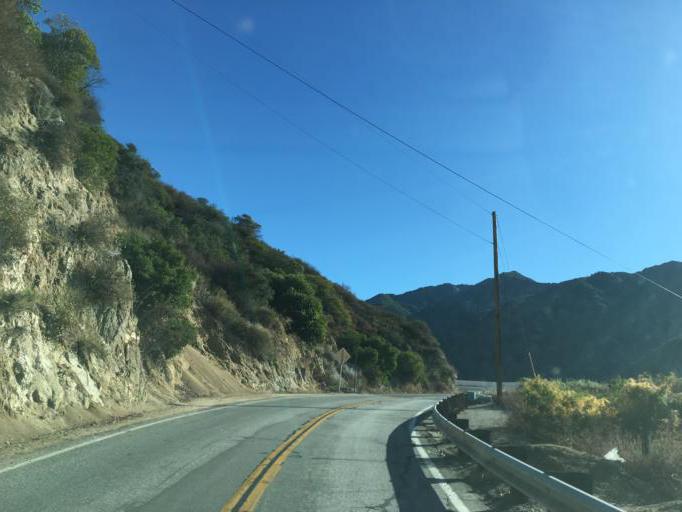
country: US
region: California
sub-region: Los Angeles County
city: Sierra Madre
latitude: 34.1791
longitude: -118.0236
